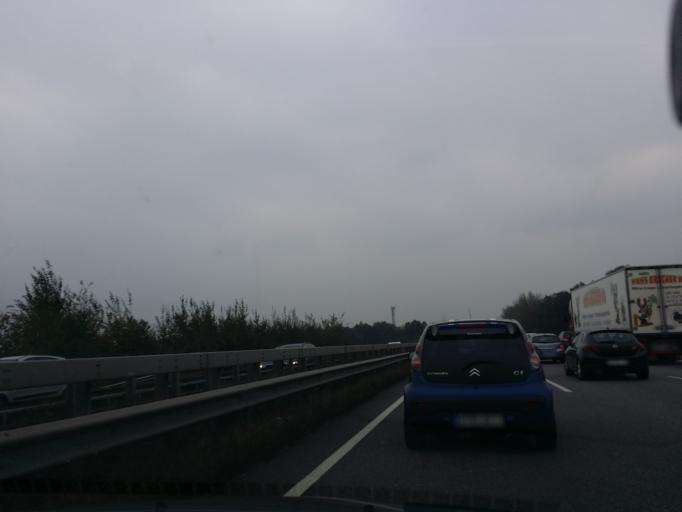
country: DE
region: Lower Saxony
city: Bakum
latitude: 52.6991
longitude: 8.1733
